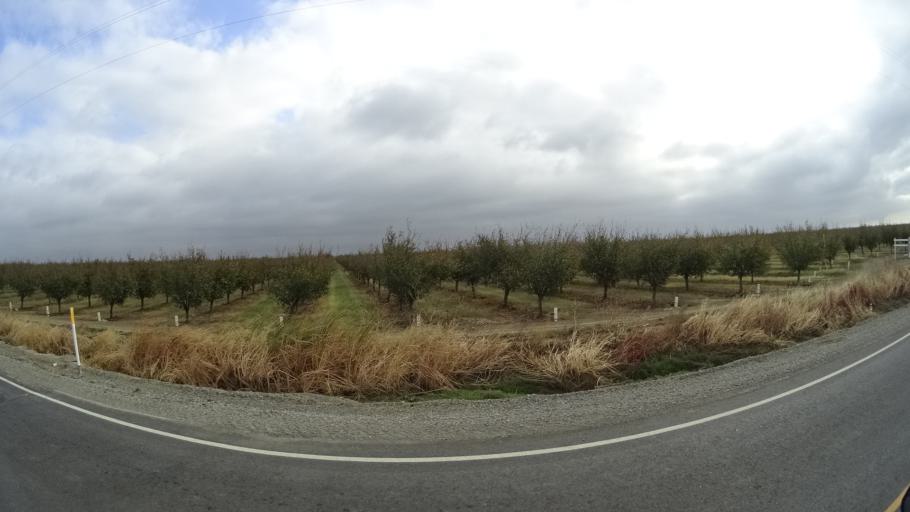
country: US
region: California
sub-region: Yolo County
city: Esparto
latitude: 38.7325
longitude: -122.0455
